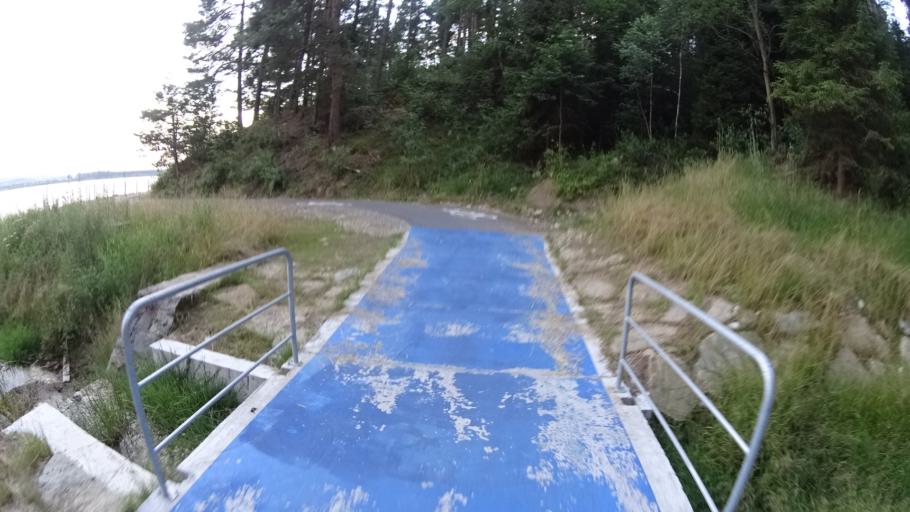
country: PL
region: Lesser Poland Voivodeship
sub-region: Powiat nowotarski
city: Frydman
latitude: 49.4635
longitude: 20.2427
